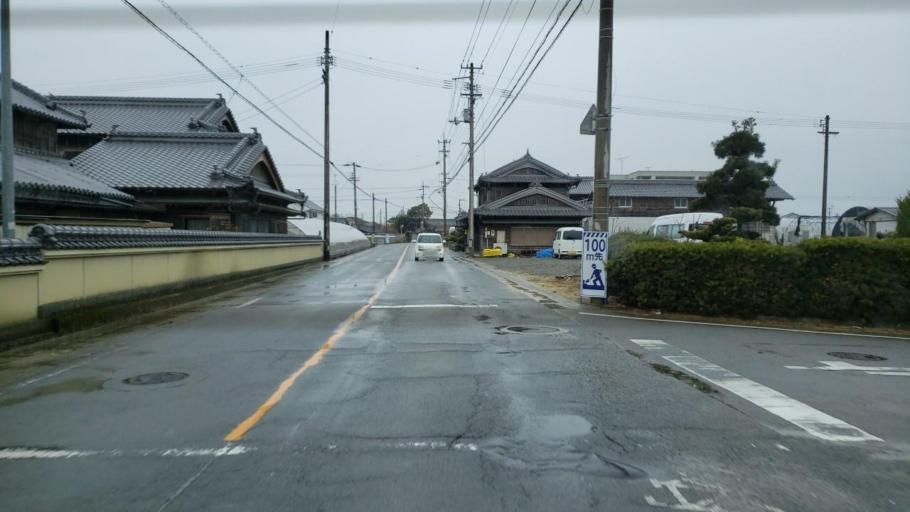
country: JP
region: Tokushima
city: Kamojimacho-jogejima
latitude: 34.0970
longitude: 134.3695
